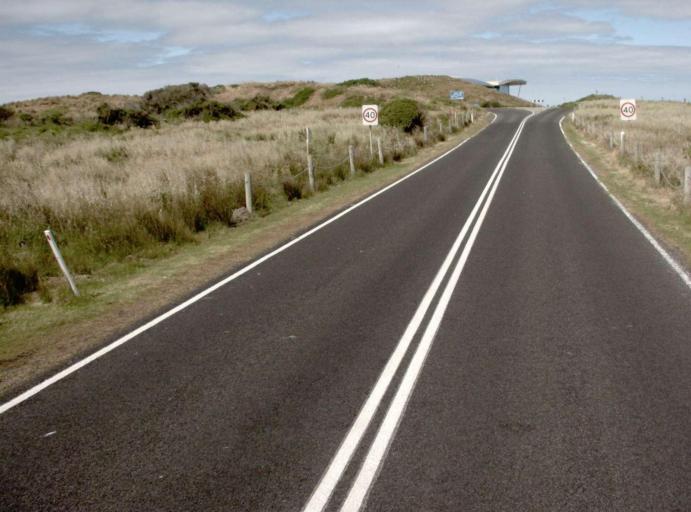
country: AU
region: Victoria
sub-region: Bass Coast
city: Phillip Island
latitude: -38.5163
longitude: 145.1201
